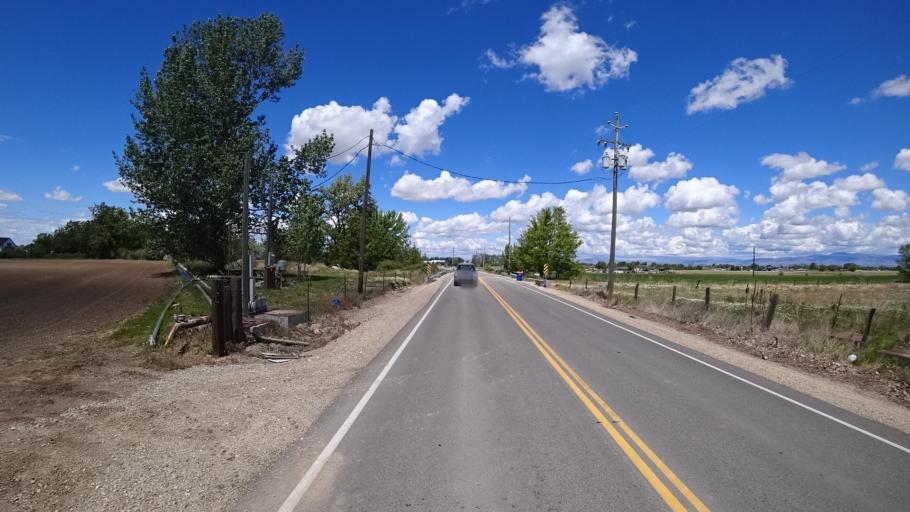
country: US
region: Idaho
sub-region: Ada County
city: Meridian
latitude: 43.5679
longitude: -116.4536
